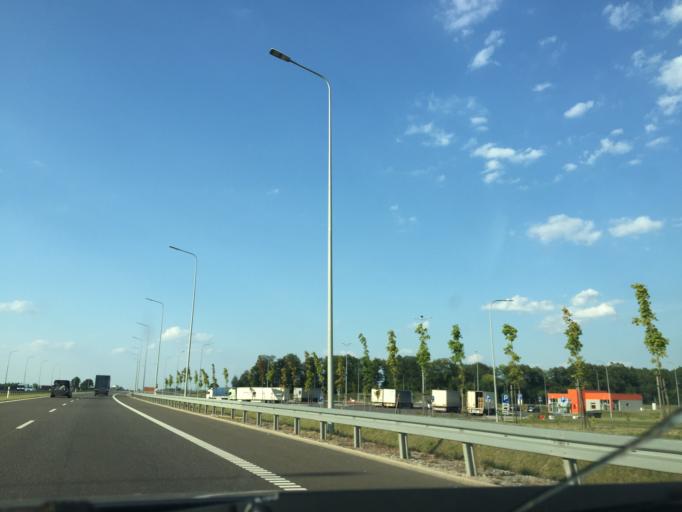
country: PL
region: Masovian Voivodeship
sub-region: Powiat radomski
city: Zakrzew
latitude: 51.4442
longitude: 21.0346
